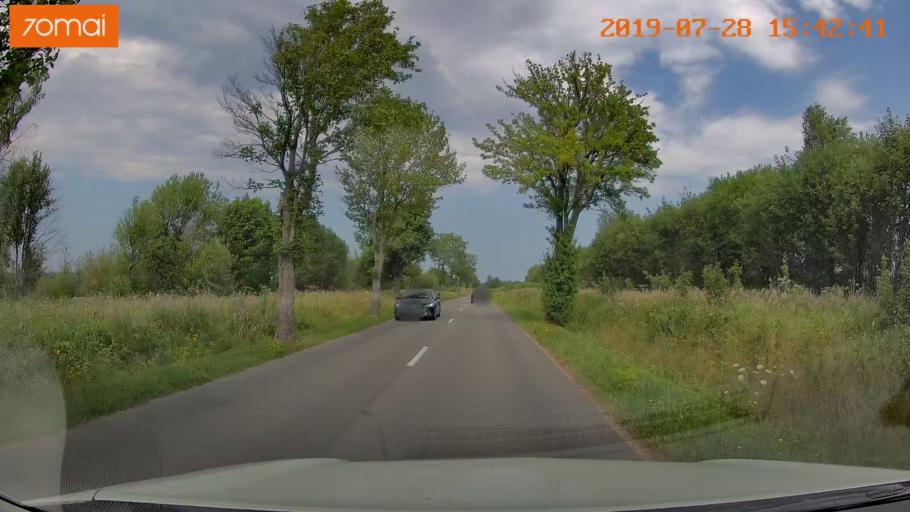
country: RU
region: Kaliningrad
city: Donskoye
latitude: 54.9325
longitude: 20.0146
